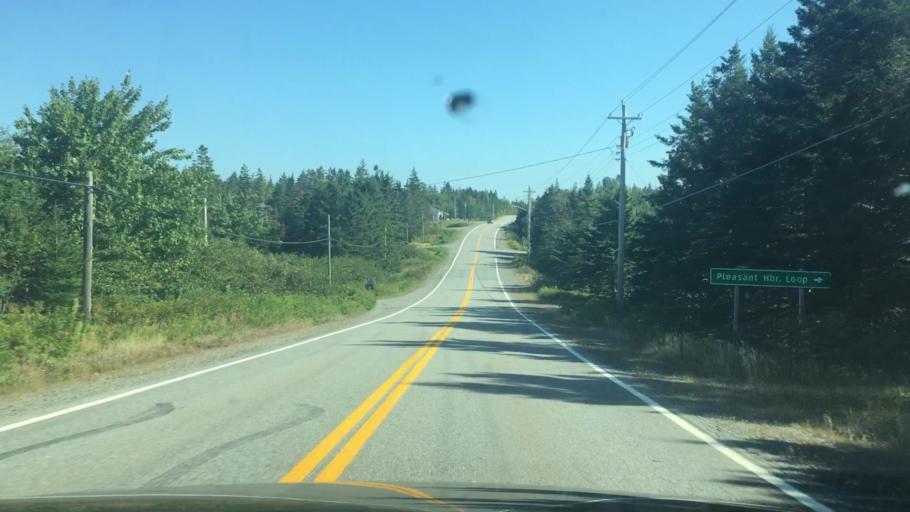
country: CA
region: Nova Scotia
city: Cole Harbour
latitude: 44.8005
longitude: -62.7145
